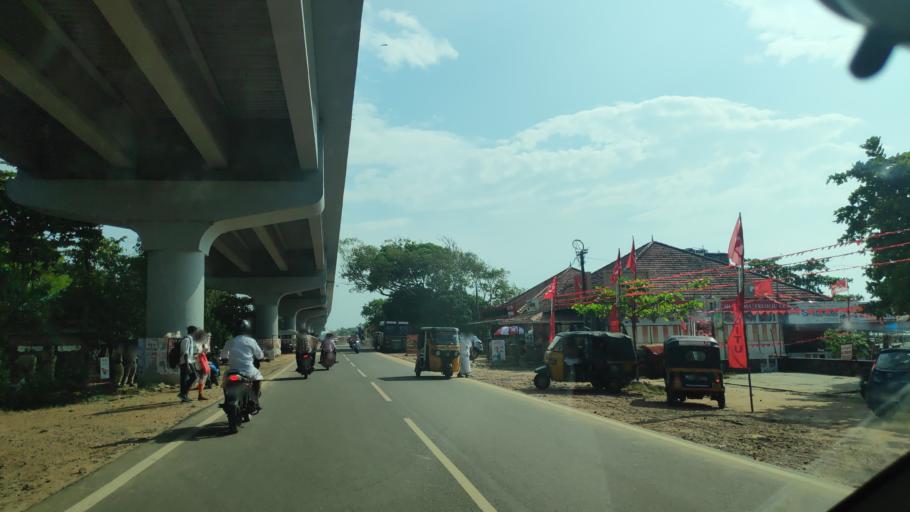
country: IN
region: Kerala
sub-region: Alappuzha
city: Alleppey
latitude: 9.4931
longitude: 76.3186
